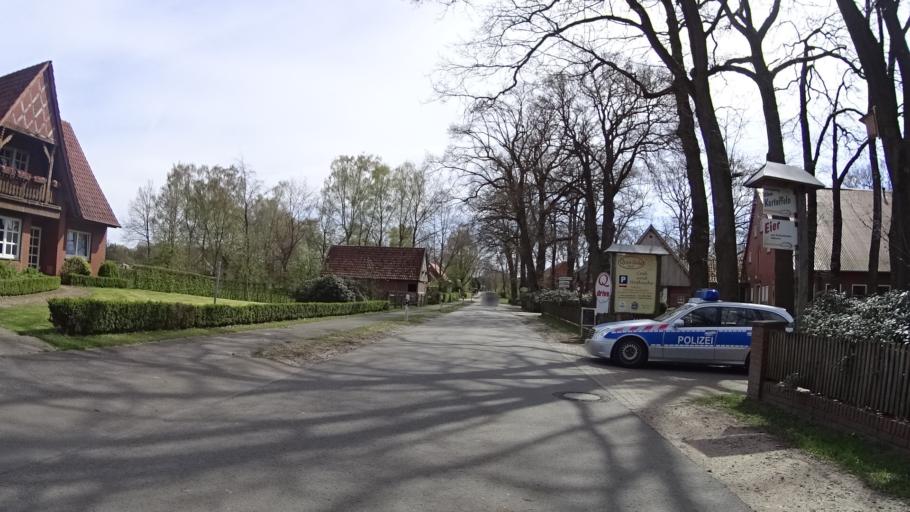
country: DE
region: Lower Saxony
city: Emsburen
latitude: 52.4482
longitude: 7.3383
